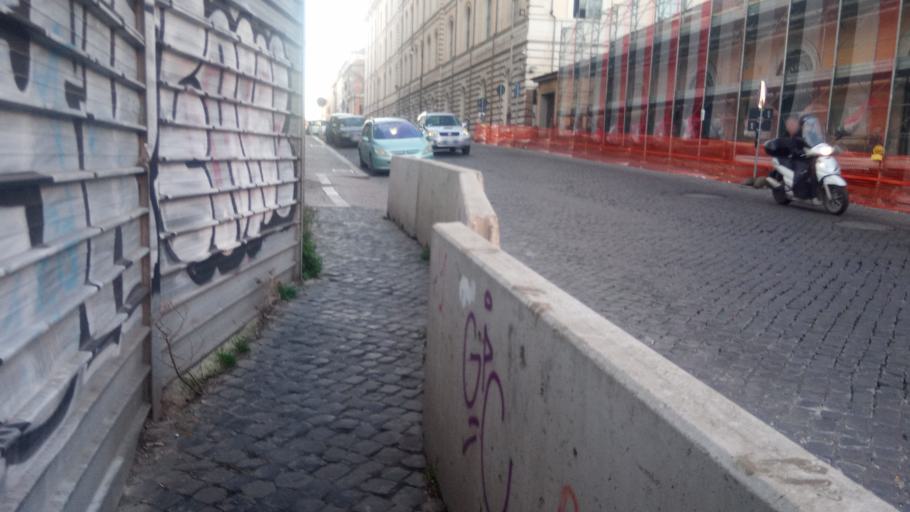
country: IT
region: Latium
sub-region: Citta metropolitana di Roma Capitale
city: Rome
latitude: 41.9001
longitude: 12.5063
